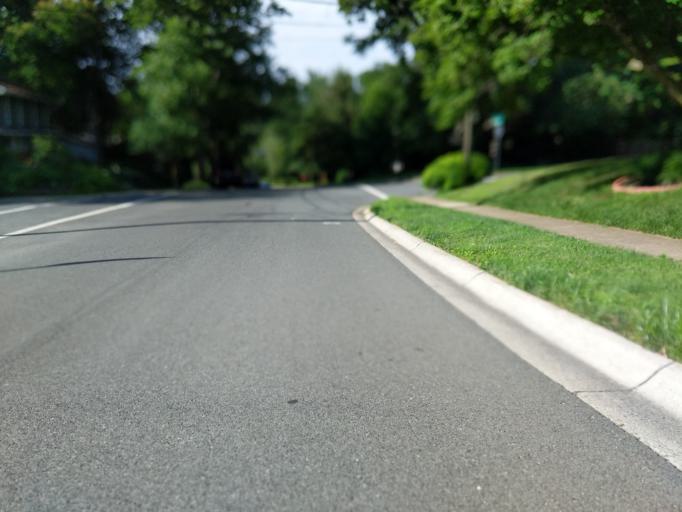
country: US
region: Maryland
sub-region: Montgomery County
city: Bethesda
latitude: 39.0078
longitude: -77.1217
